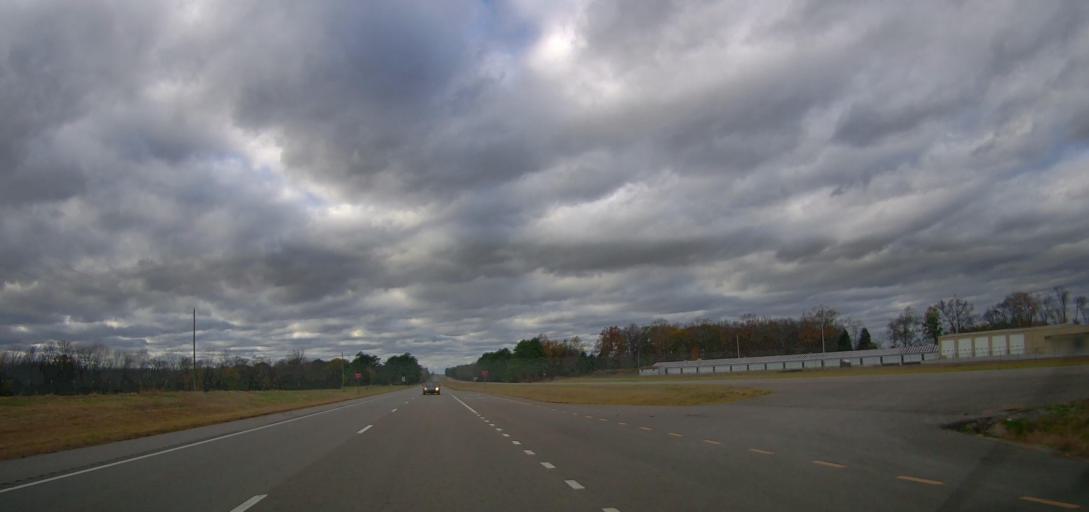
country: US
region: Alabama
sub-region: Morgan County
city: Danville
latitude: 34.3447
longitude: -87.0336
